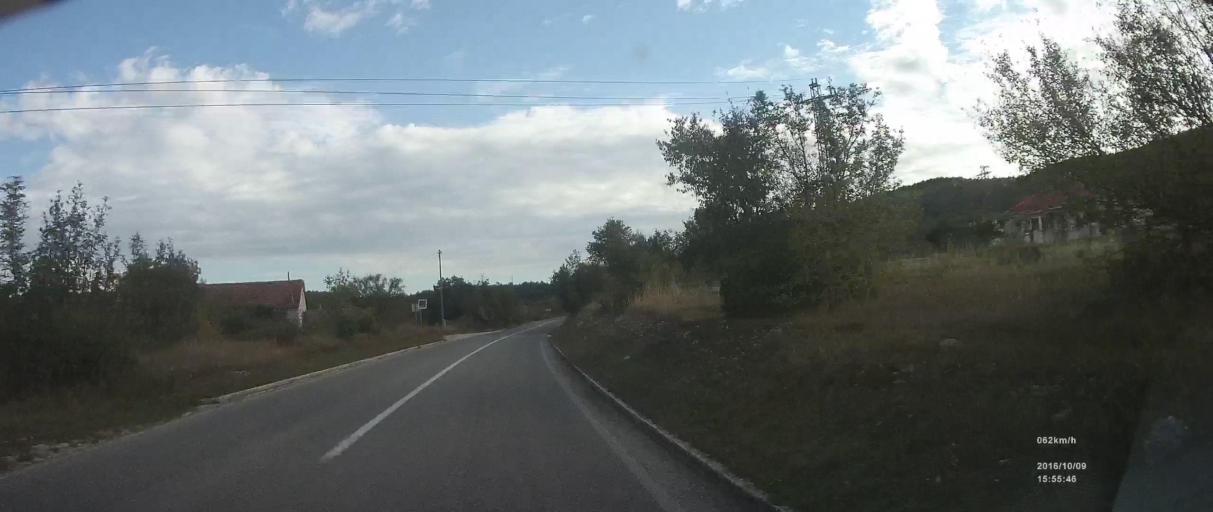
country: HR
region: Splitsko-Dalmatinska
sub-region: Grad Trogir
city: Trogir
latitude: 43.5840
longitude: 16.2321
